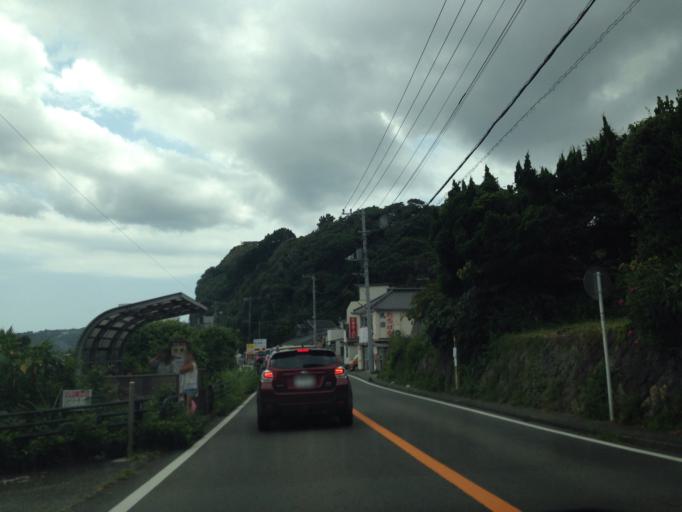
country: JP
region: Shizuoka
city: Shimoda
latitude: 34.7030
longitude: 138.9761
